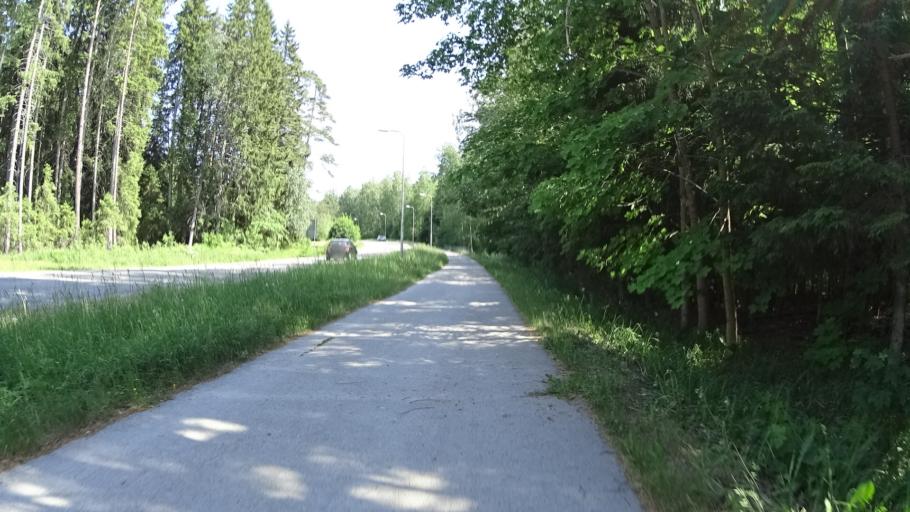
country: FI
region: Uusimaa
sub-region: Raaseporin
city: Karis
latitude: 60.0808
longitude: 23.6644
